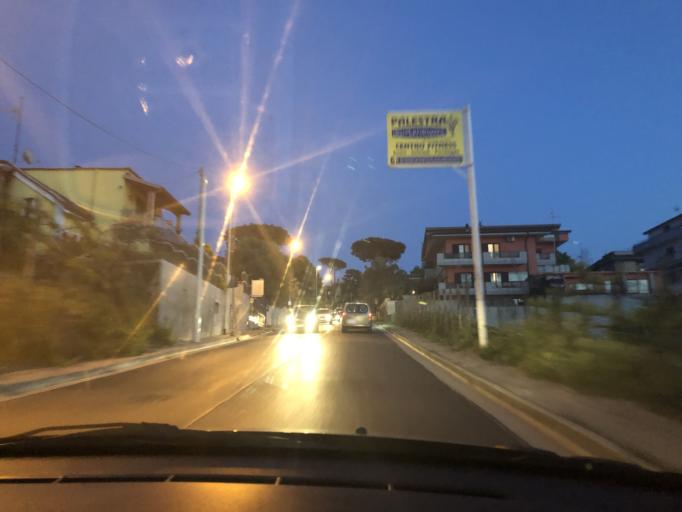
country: IT
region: Campania
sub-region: Provincia di Napoli
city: Marano di Napoli
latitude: 40.8886
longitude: 14.1795
